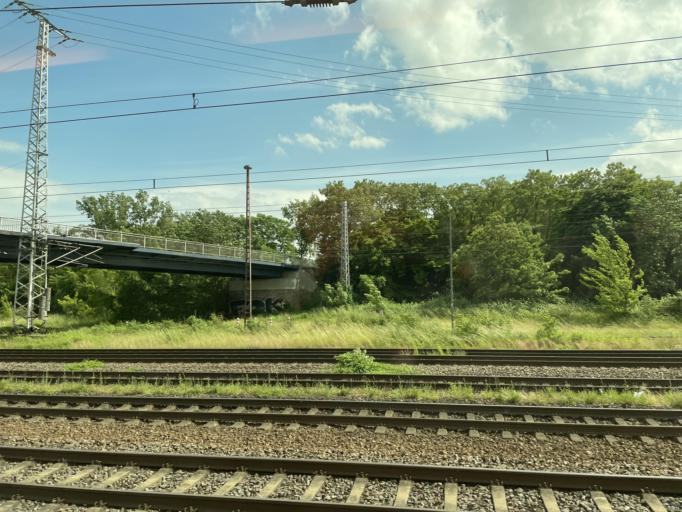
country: DE
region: Saxony-Anhalt
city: Stendal
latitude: 52.5932
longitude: 11.8366
